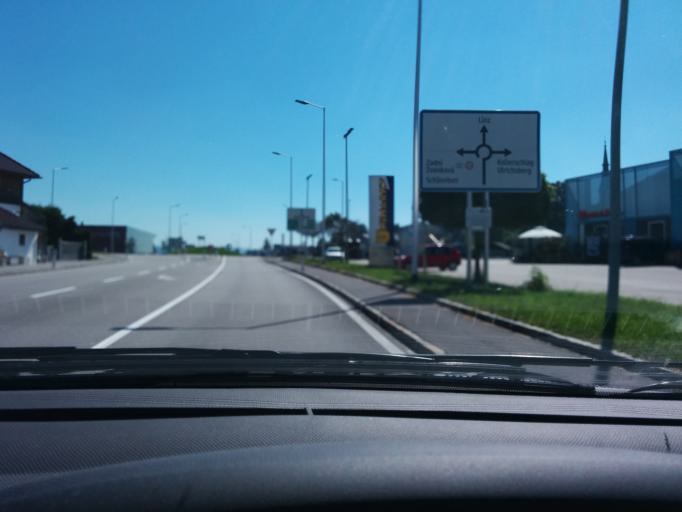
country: AT
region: Upper Austria
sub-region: Politischer Bezirk Rohrbach
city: Ulrichsberg
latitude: 48.6785
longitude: 13.9089
